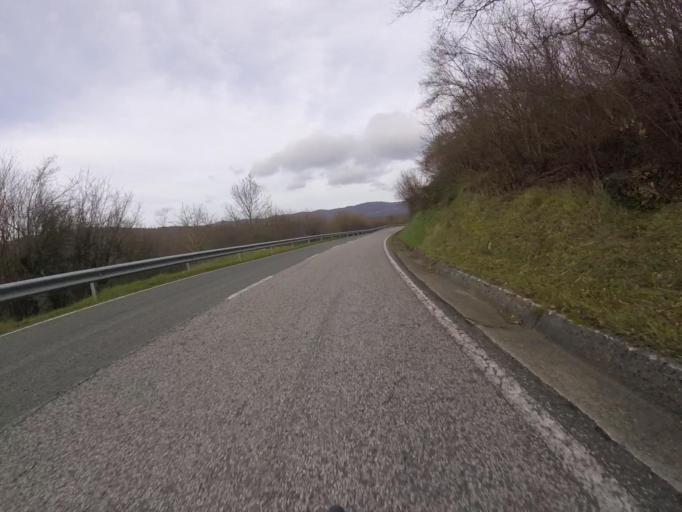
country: ES
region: Navarre
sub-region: Provincia de Navarra
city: Olazagutia
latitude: 42.8681
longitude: -2.1867
